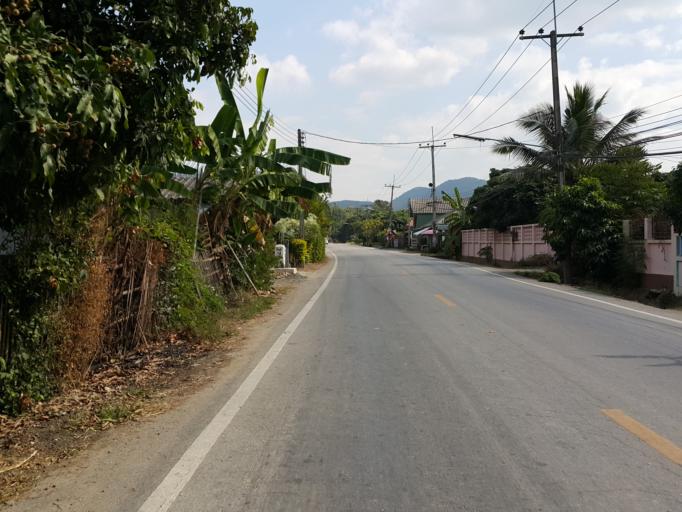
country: TH
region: Chiang Mai
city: San Kamphaeng
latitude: 18.7245
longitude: 99.1672
